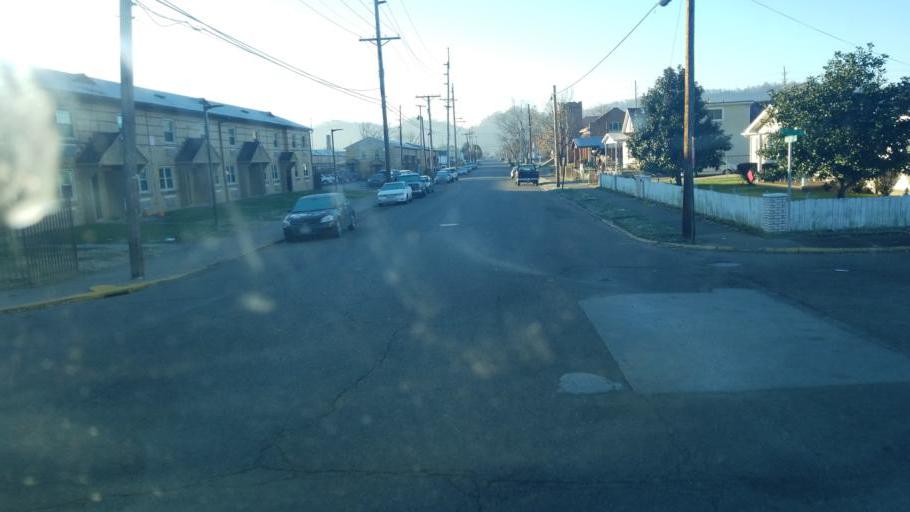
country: US
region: Ohio
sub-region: Scioto County
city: Portsmouth
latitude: 38.7437
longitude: -82.9888
